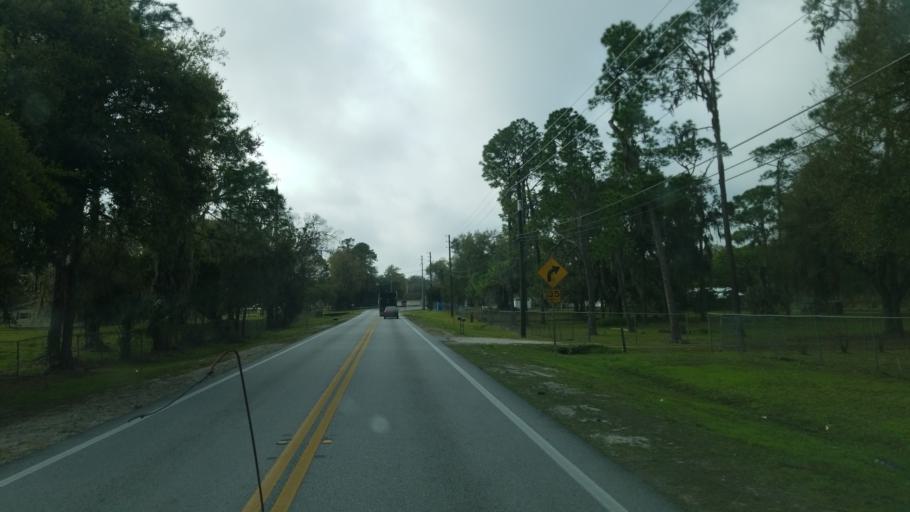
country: US
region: Florida
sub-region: Polk County
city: Winston
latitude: 28.0612
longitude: -82.0065
